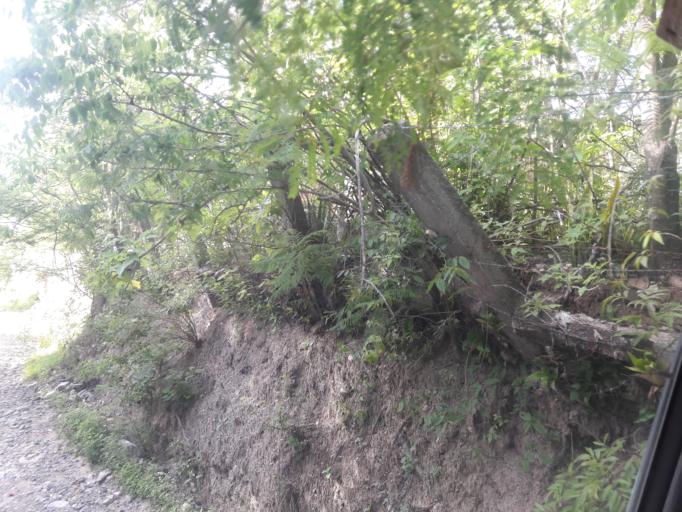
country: MX
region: Oaxaca
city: Ciudad de Huajuapam de Leon
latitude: 17.8406
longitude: -97.7913
